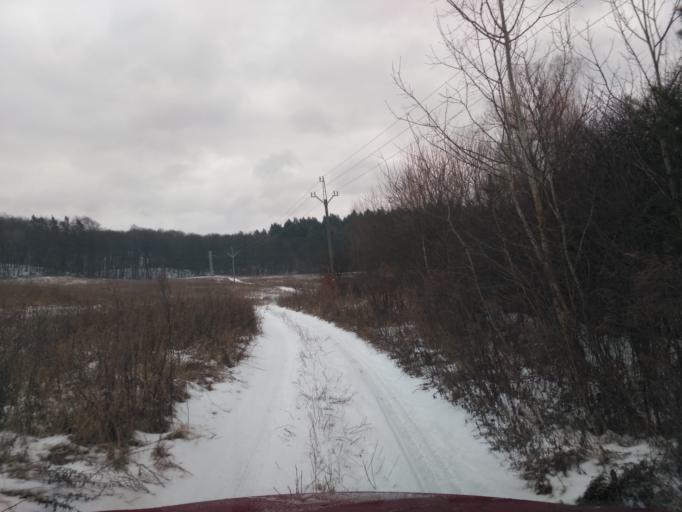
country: SK
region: Presovsky
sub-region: Okres Presov
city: Presov
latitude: 48.9995
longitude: 21.1785
